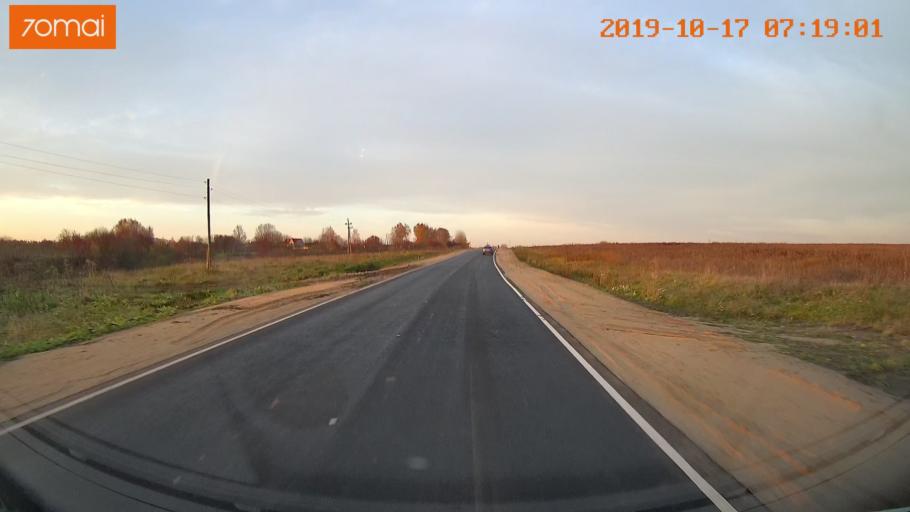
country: RU
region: Ivanovo
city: Gavrilov Posad
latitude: 56.3481
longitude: 40.2079
